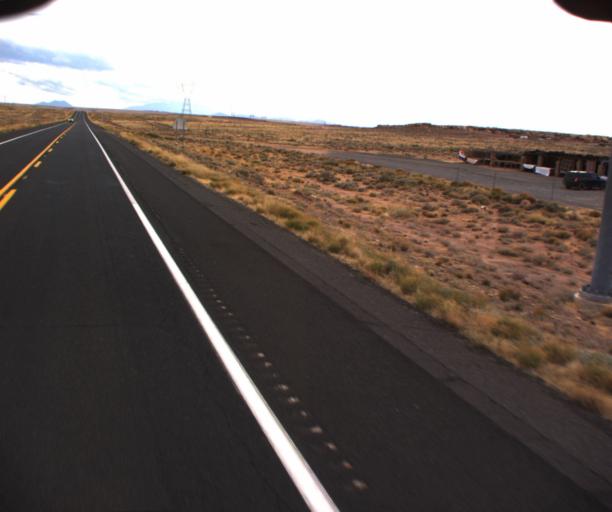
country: US
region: Arizona
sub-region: Coconino County
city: Tuba City
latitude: 35.8216
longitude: -111.4406
